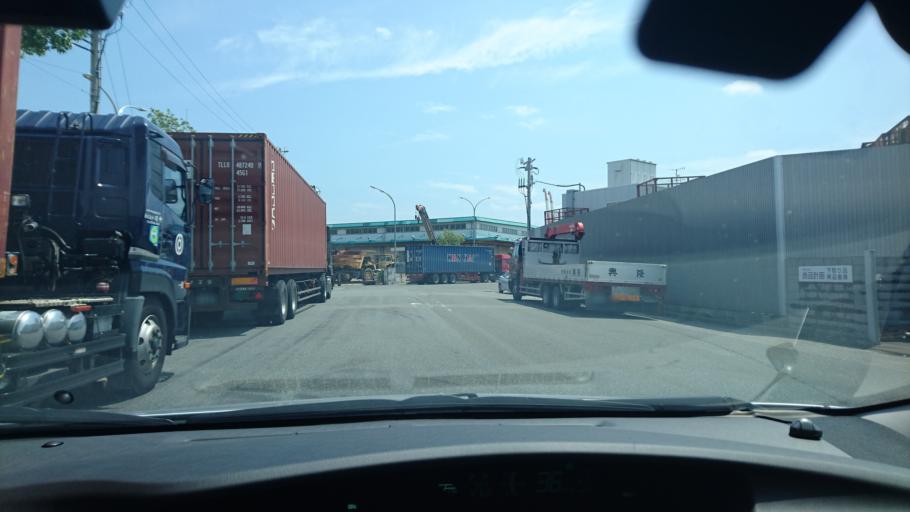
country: JP
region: Hyogo
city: Kobe
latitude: 34.6742
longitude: 135.2288
